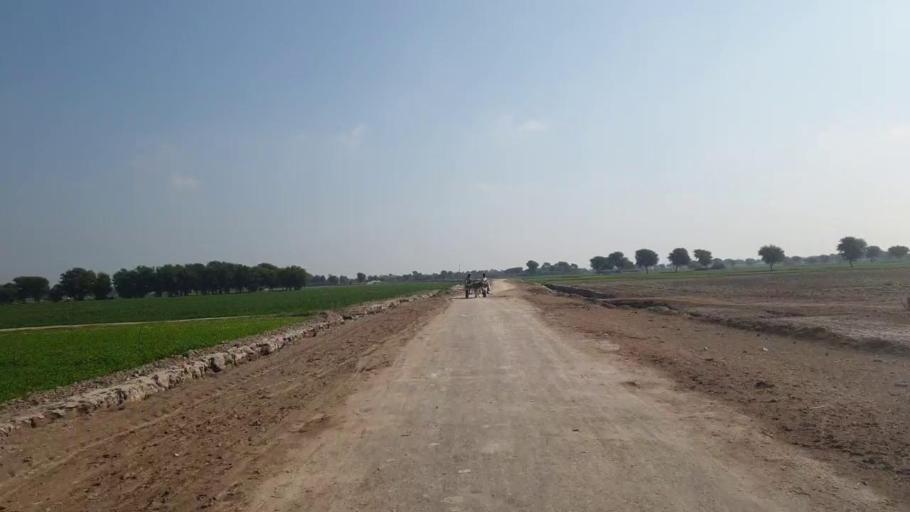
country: PK
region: Sindh
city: Shahdadpur
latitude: 26.0298
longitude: 68.6210
